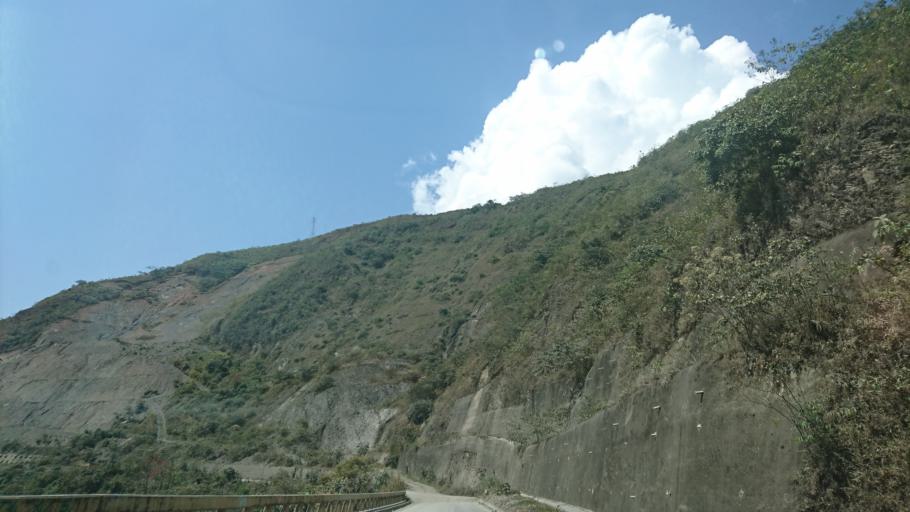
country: BO
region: La Paz
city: Coroico
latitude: -16.2105
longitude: -67.7926
